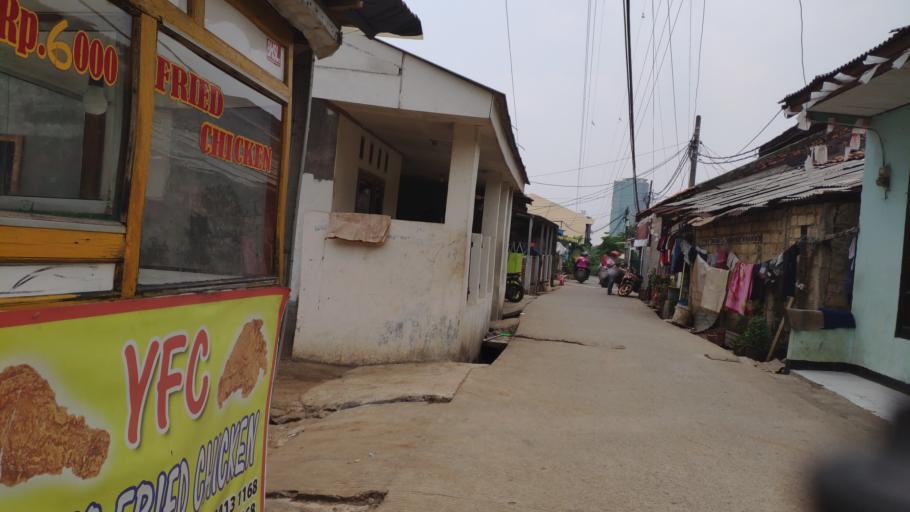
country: ID
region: West Java
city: Depok
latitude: -6.3081
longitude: 106.8318
